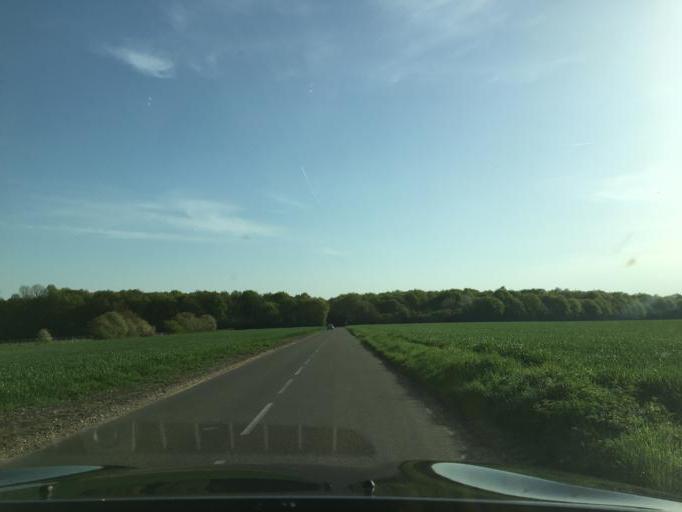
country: FR
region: Ile-de-France
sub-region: Departement des Yvelines
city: Conde-sur-Vesgre
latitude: 48.7278
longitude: 1.6575
